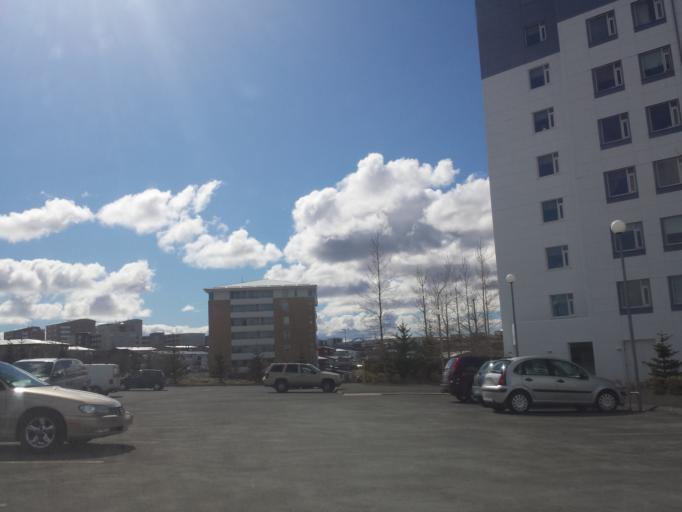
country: IS
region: Capital Region
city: Reykjavik
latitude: 64.0951
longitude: -21.8533
